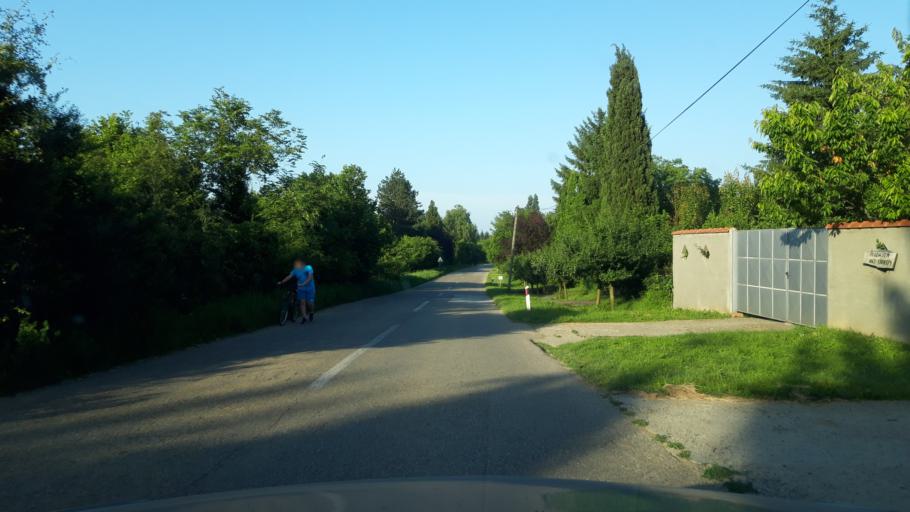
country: RS
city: Glozan
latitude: 45.2057
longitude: 19.5830
